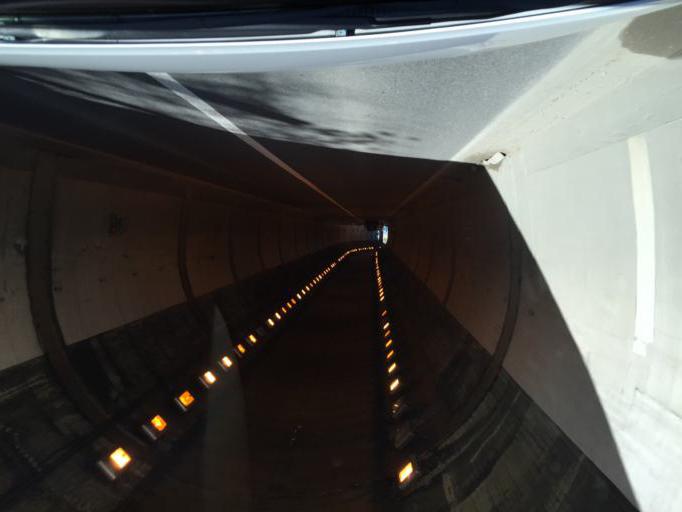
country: JP
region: Fukushima
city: Iwaki
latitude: 37.1173
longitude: 140.9992
